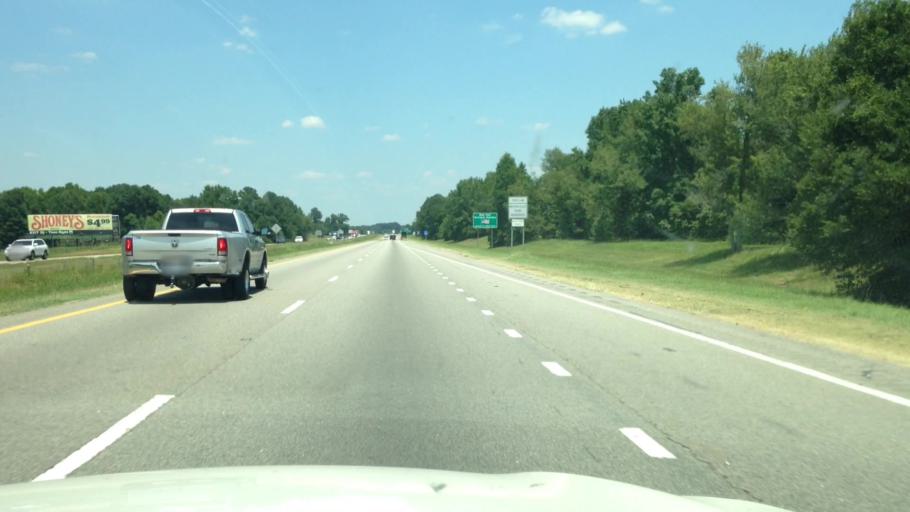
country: US
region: North Carolina
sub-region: Robeson County
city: Rowland
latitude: 34.5057
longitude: -79.3024
